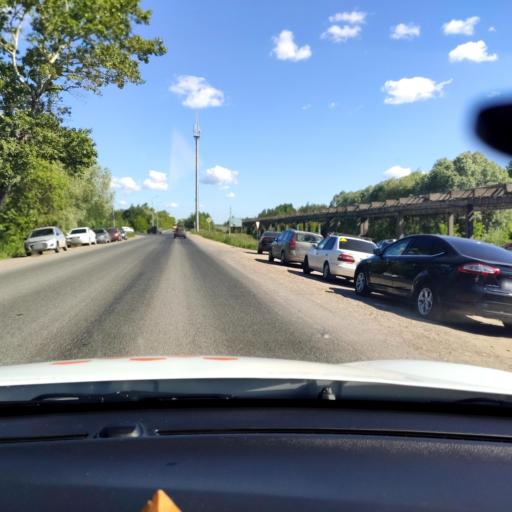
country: RU
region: Tatarstan
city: Staroye Arakchino
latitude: 55.8809
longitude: 48.9761
